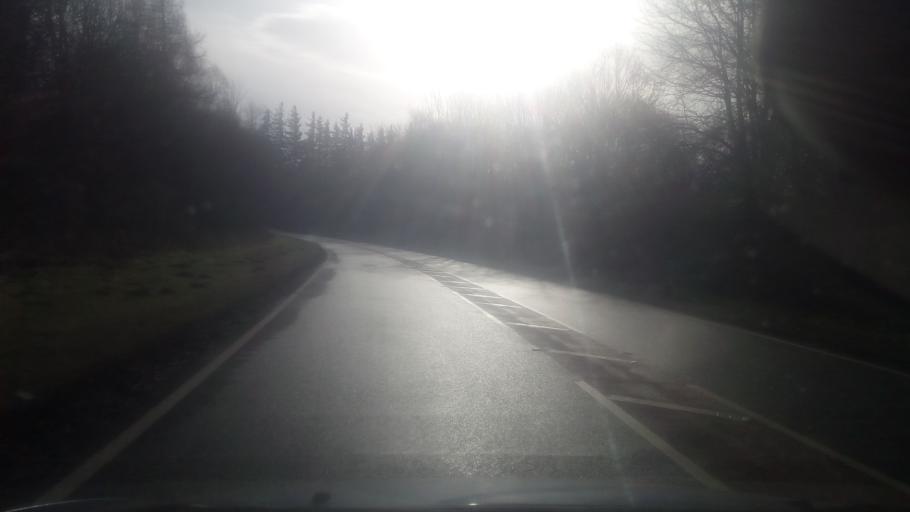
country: GB
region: Scotland
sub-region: The Scottish Borders
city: Jedburgh
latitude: 55.4357
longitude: -2.5416
